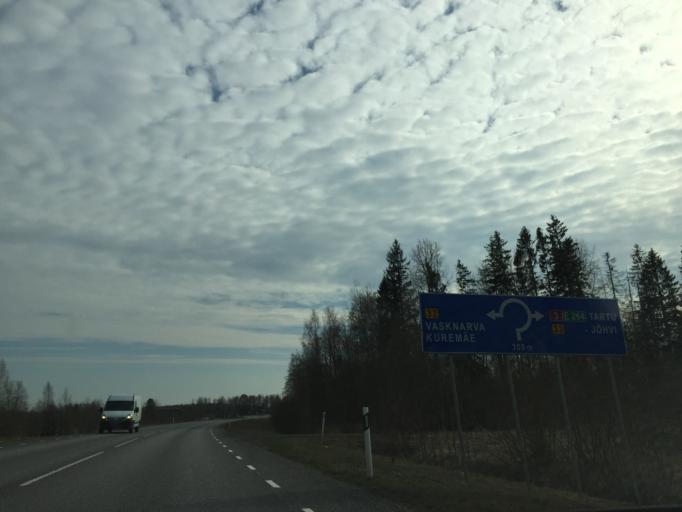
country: EE
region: Ida-Virumaa
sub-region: Johvi vald
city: Johvi
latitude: 59.3415
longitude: 27.4680
